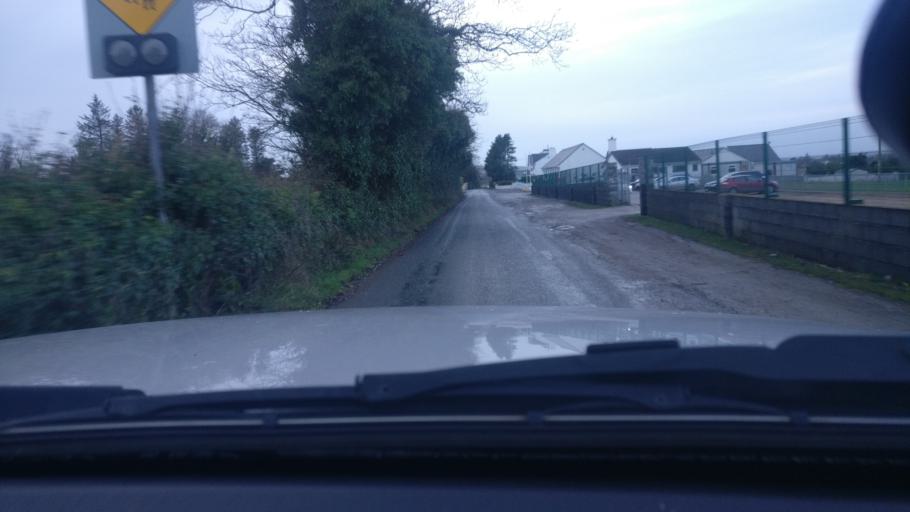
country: IE
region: Connaught
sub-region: County Galway
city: Loughrea
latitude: 53.1636
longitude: -8.5618
